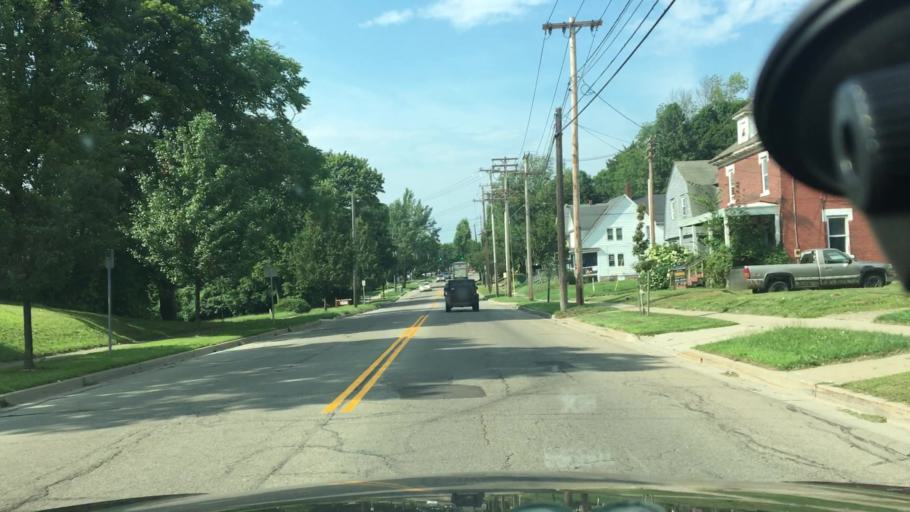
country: US
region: New York
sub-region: Chautauqua County
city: Jamestown
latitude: 42.1066
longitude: -79.2413
